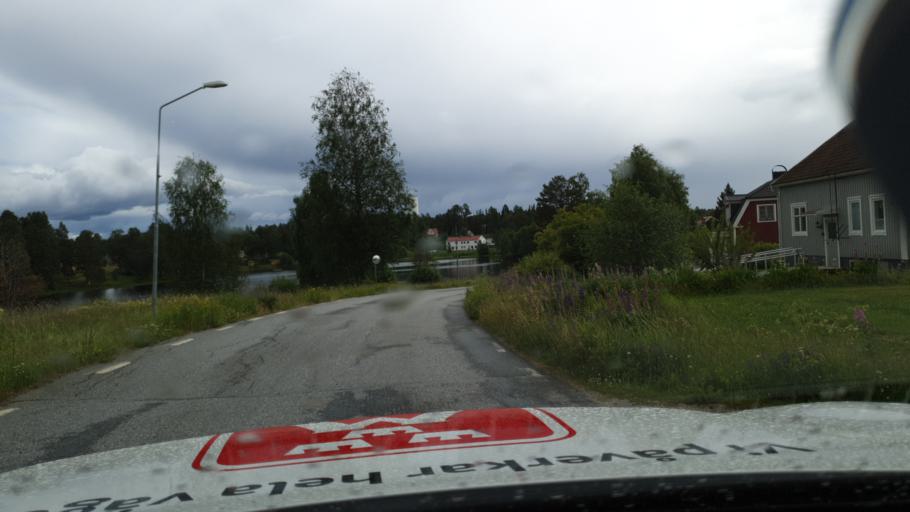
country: SE
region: Vaesterbotten
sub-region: Dorotea Kommun
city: Dorotea
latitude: 63.8142
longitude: 16.4040
